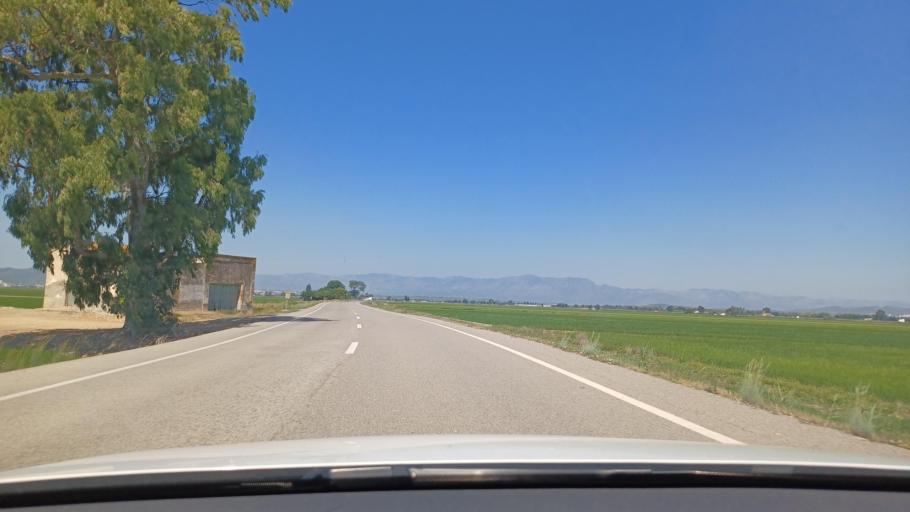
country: ES
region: Catalonia
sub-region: Provincia de Tarragona
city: Deltebre
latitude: 40.7035
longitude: 0.6601
